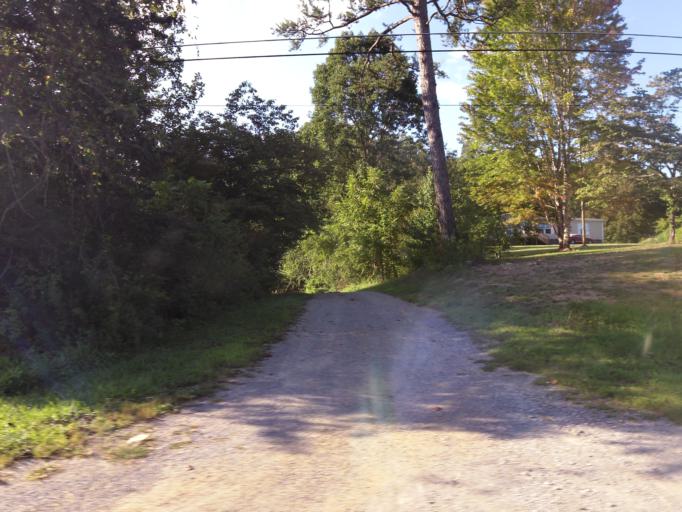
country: US
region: Tennessee
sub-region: Union County
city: Maynardville
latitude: 36.2221
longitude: -83.7791
